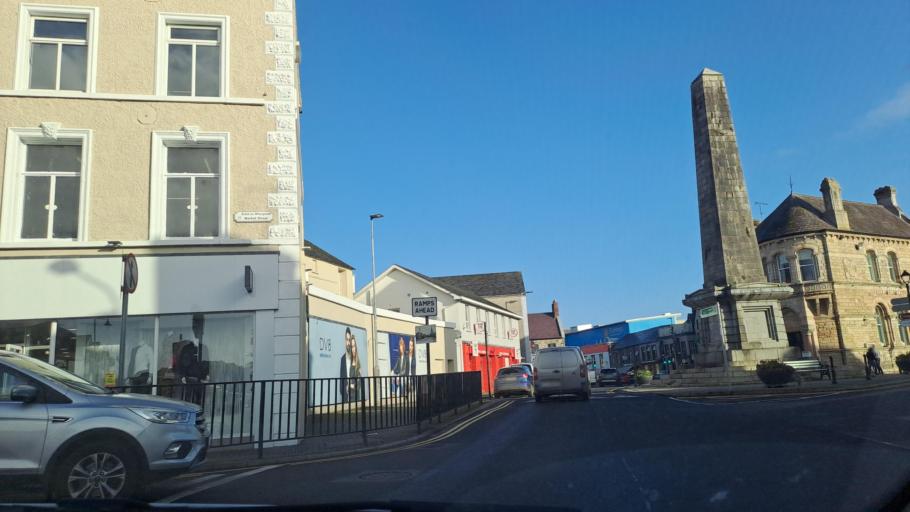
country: IE
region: Ulster
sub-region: County Monaghan
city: Monaghan
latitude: 54.2476
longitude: -6.9709
